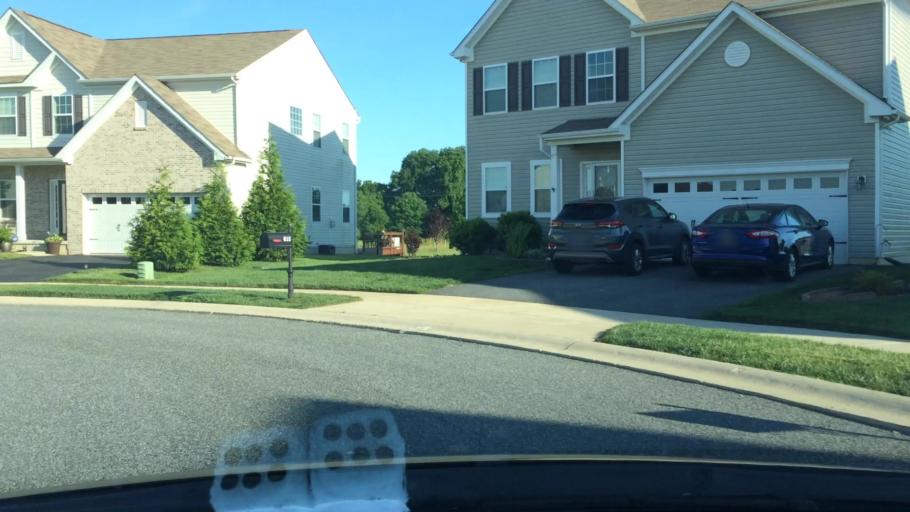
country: US
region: Delaware
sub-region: New Castle County
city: Delaware City
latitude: 39.5409
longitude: -75.6596
